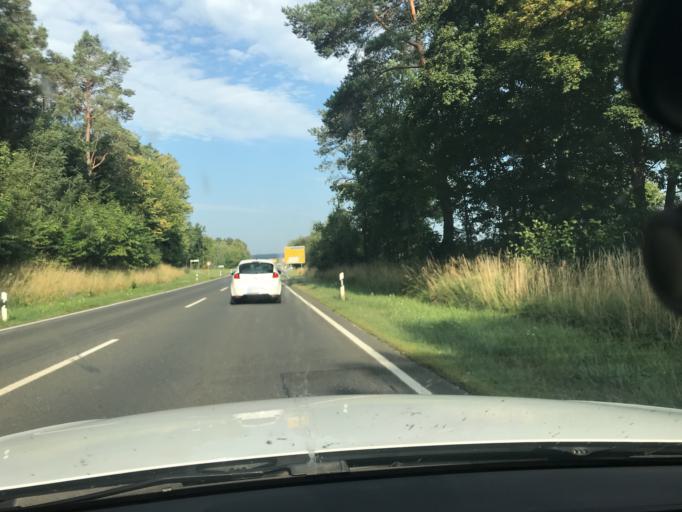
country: DE
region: Bavaria
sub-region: Upper Palatinate
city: Auerbach
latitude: 49.6994
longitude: 11.6108
